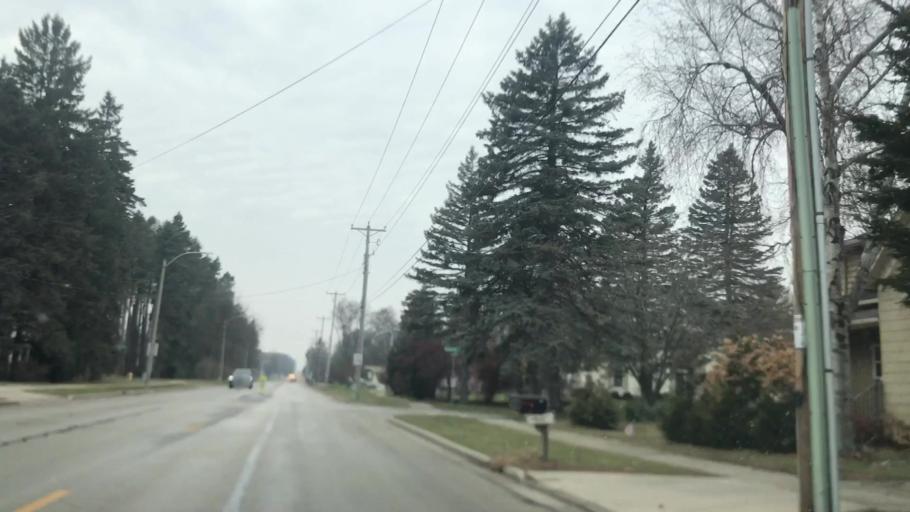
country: US
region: Wisconsin
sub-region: Ozaukee County
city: Cedarburg
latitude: 43.2937
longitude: -87.9992
